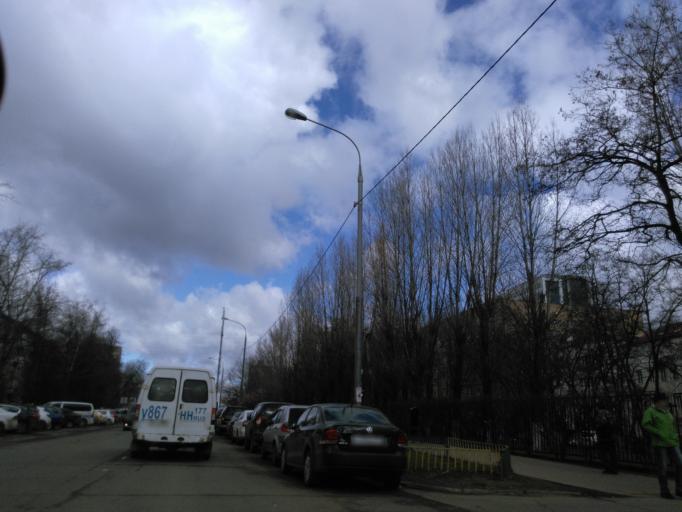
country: RU
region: Moskovskaya
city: Levoberezhnyy
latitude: 55.8361
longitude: 37.4893
